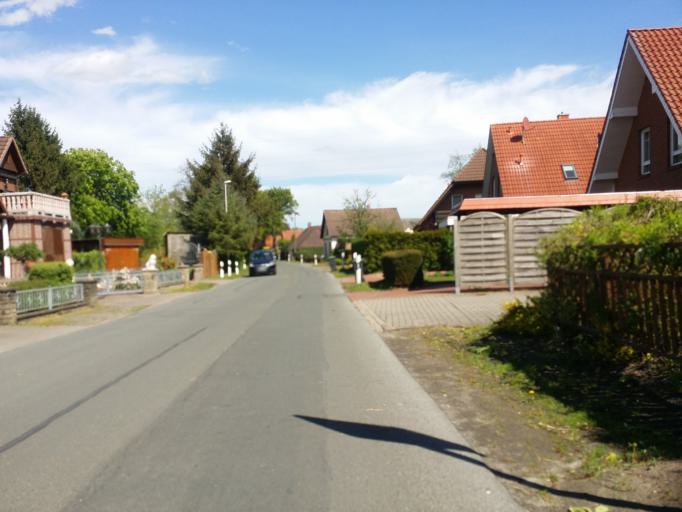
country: DE
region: Lower Saxony
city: Delmenhorst
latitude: 53.0700
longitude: 8.6549
